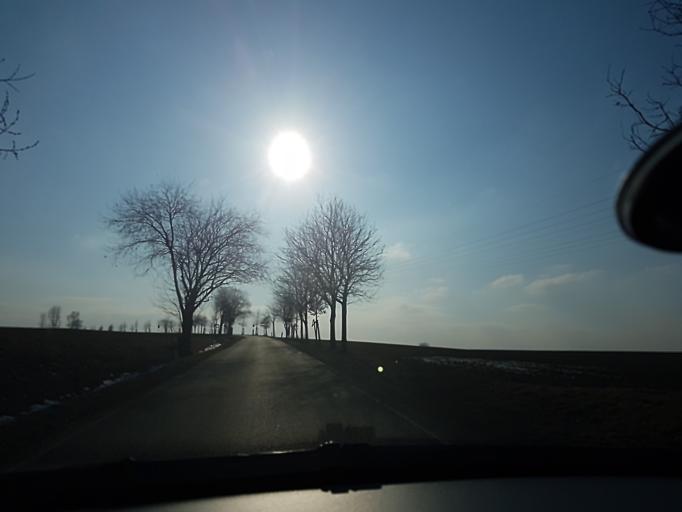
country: DE
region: Saxony
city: Oberschona
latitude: 50.9152
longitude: 13.3007
